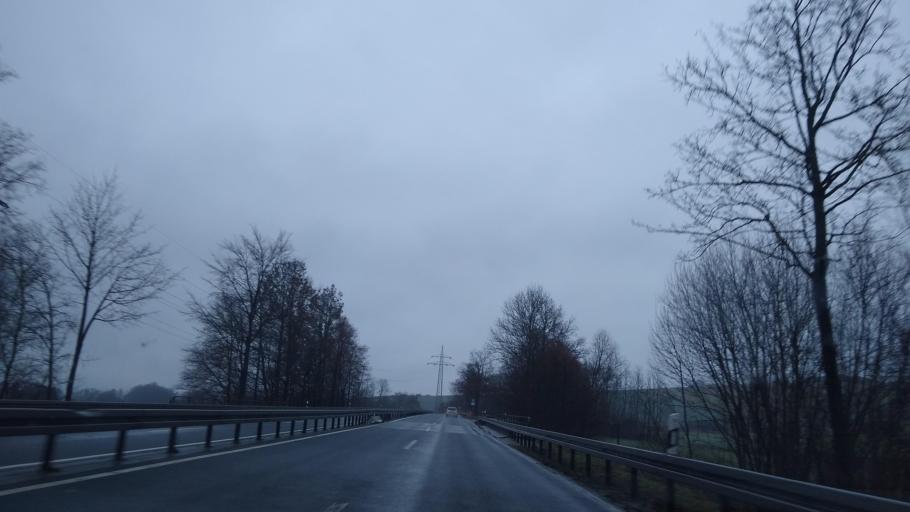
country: DE
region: Lower Saxony
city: Gittelde
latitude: 51.7961
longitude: 10.1961
